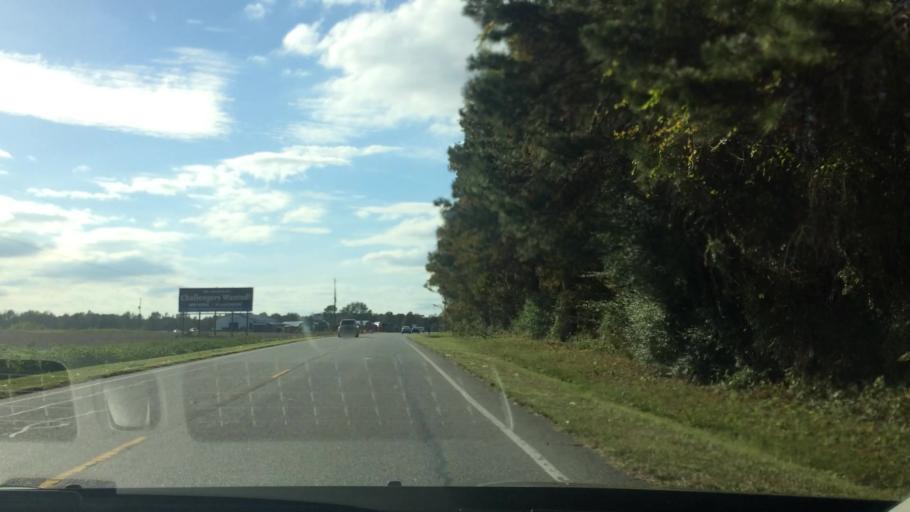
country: US
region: North Carolina
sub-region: Wayne County
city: Elroy
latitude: 35.4411
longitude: -77.8221
